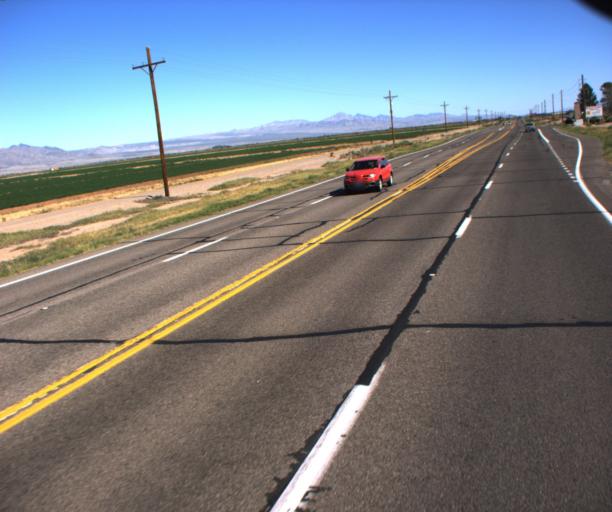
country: US
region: Arizona
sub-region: Mohave County
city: Mohave Valley
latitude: 34.9299
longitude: -114.5978
